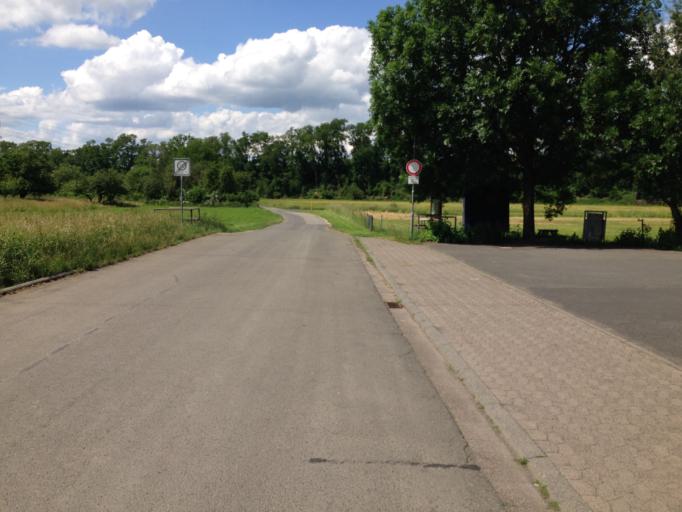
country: DE
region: Hesse
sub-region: Regierungsbezirk Giessen
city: Heuchelheim
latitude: 50.5622
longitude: 8.6425
